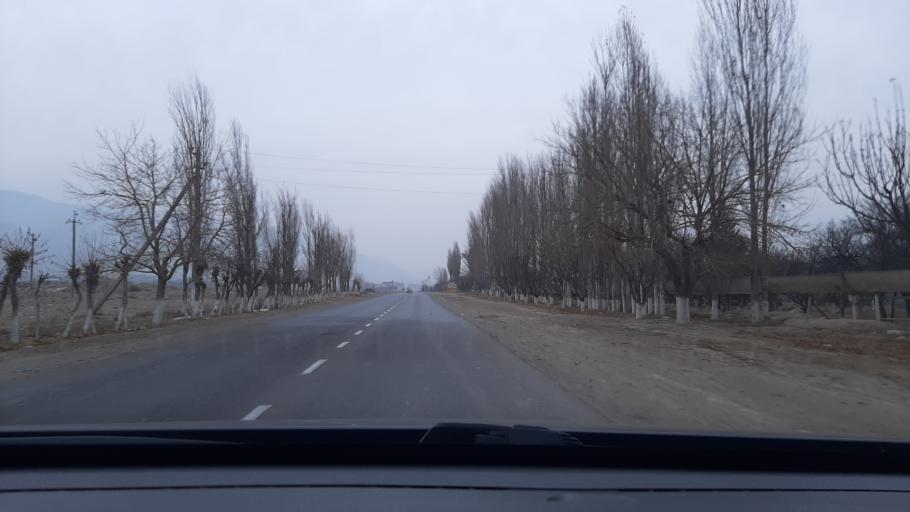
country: TJ
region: Viloyati Sughd
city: Khujand
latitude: 40.2712
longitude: 69.5747
